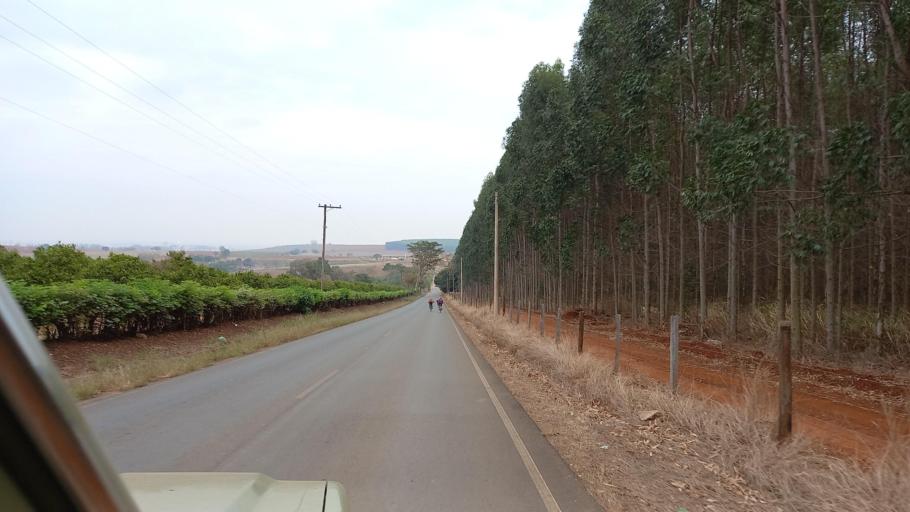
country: BR
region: Sao Paulo
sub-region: Moji-Guacu
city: Mogi-Gaucu
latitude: -22.3304
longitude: -46.8725
